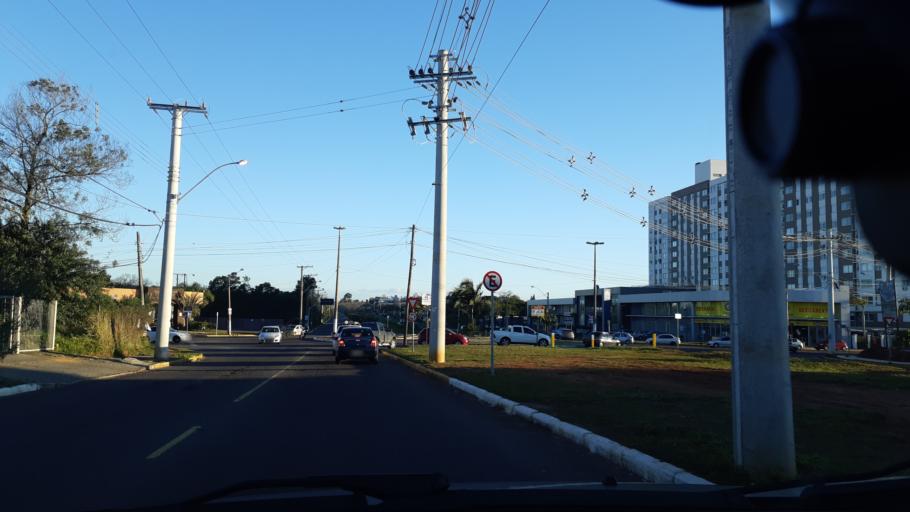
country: BR
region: Rio Grande do Sul
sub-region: Canoas
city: Canoas
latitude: -29.9178
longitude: -51.1546
